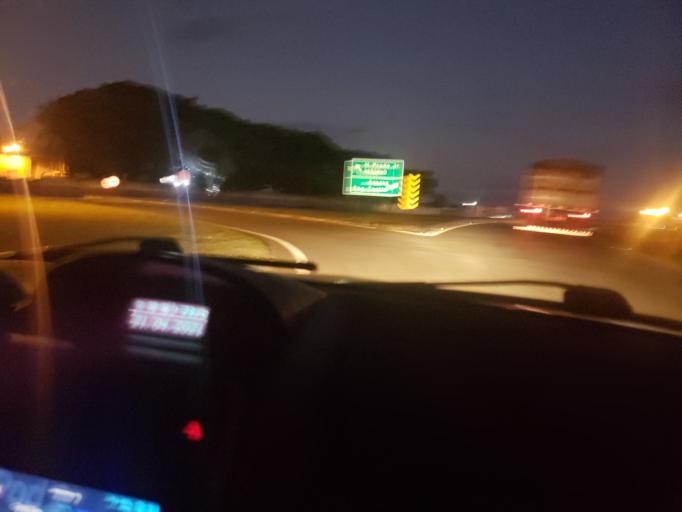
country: BR
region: Sao Paulo
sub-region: Conchal
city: Conchal
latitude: -22.3439
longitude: -47.1582
